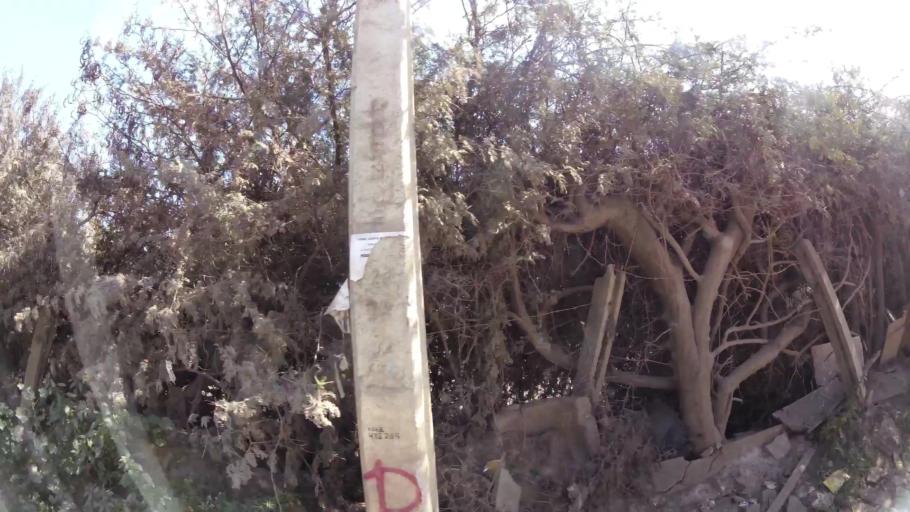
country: CL
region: Santiago Metropolitan
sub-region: Provincia de Talagante
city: Penaflor
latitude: -33.5785
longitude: -70.8128
